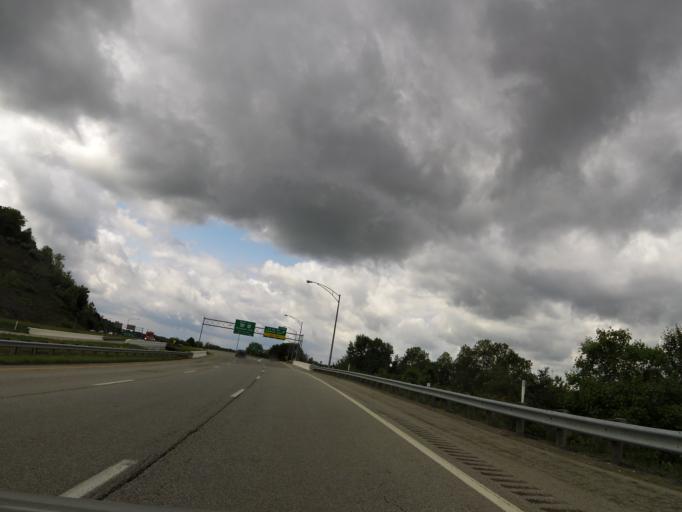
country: US
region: Ohio
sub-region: Athens County
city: Athens
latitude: 39.3303
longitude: -82.0851
